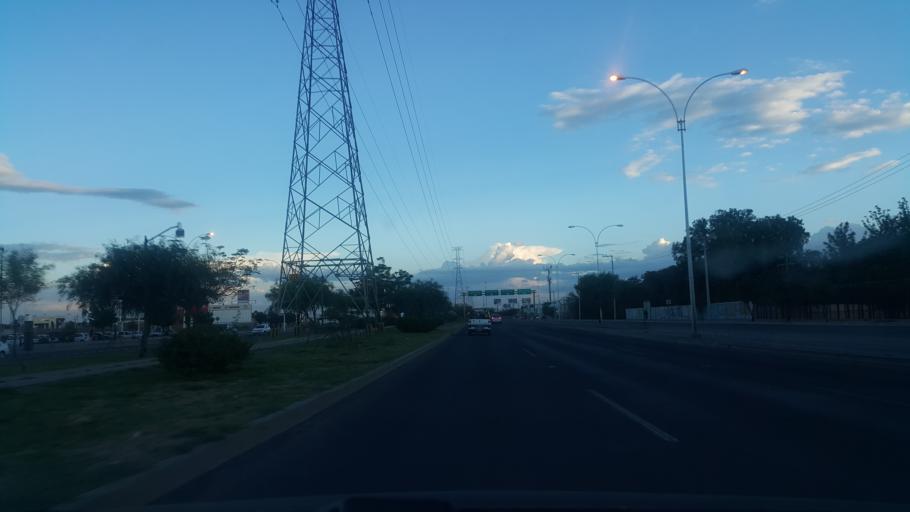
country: MX
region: Guanajuato
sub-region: Leon
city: Medina
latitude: 21.1228
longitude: -101.6280
